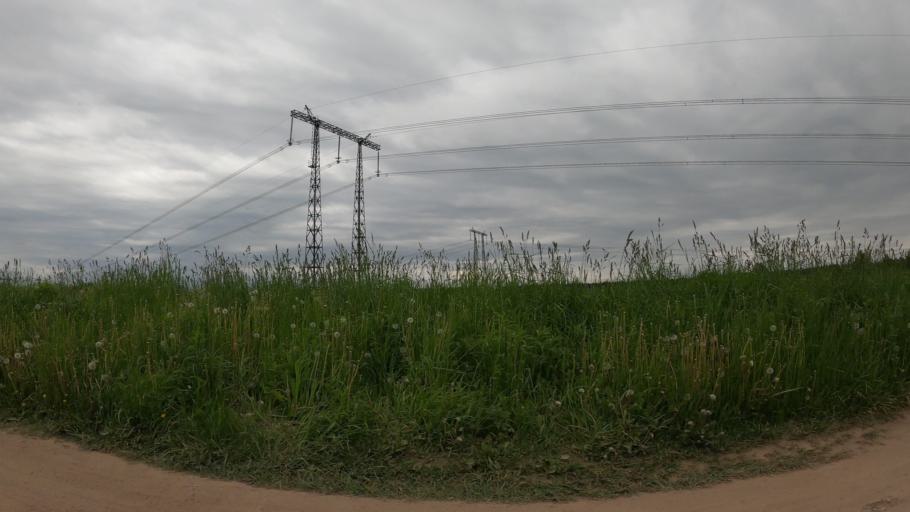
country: RU
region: Moskovskaya
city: Lesnyye Polyany
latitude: 55.9587
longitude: 37.8808
